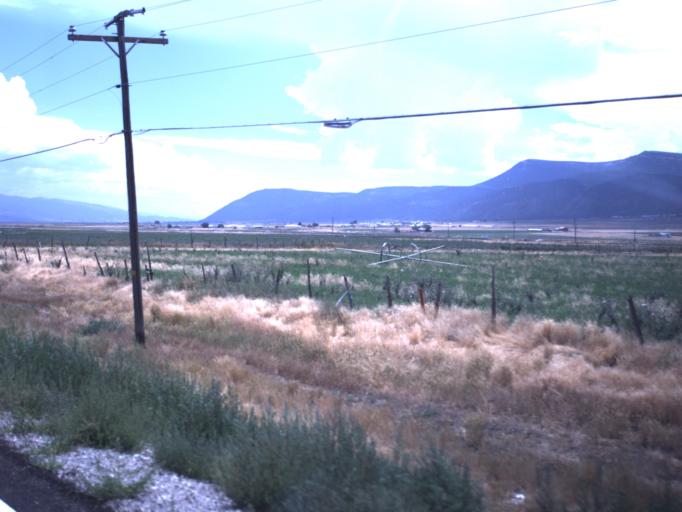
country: US
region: Utah
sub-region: Sanpete County
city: Fountain Green
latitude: 39.5914
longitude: -111.6173
